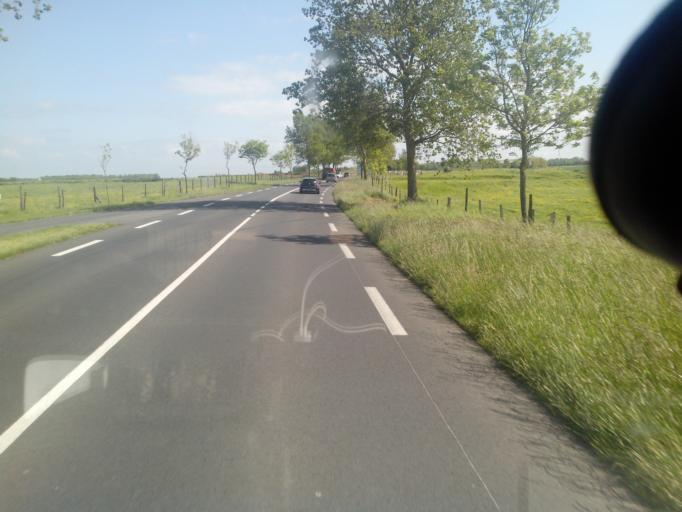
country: FR
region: Lower Normandy
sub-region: Departement du Calvados
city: Courseulles-sur-Mer
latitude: 49.3072
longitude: -0.4396
